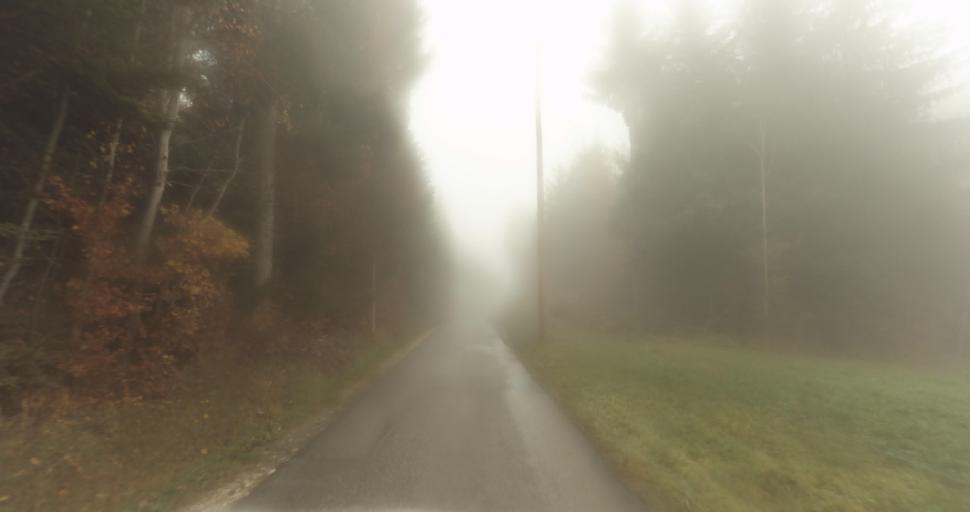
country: FR
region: Rhone-Alpes
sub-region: Departement de la Haute-Savoie
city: Thorens-Glieres
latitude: 45.9788
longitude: 6.2122
